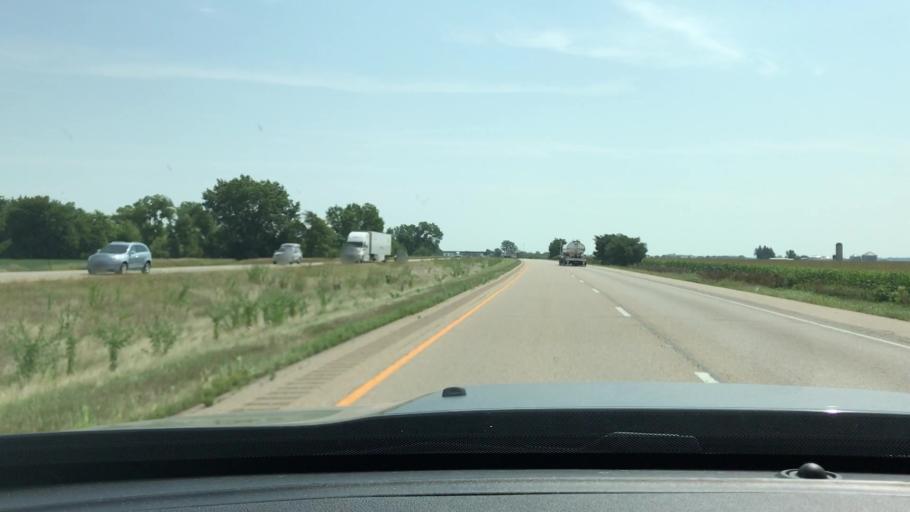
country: US
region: Illinois
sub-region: Henry County
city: Kewanee
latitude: 41.3863
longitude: -89.8120
